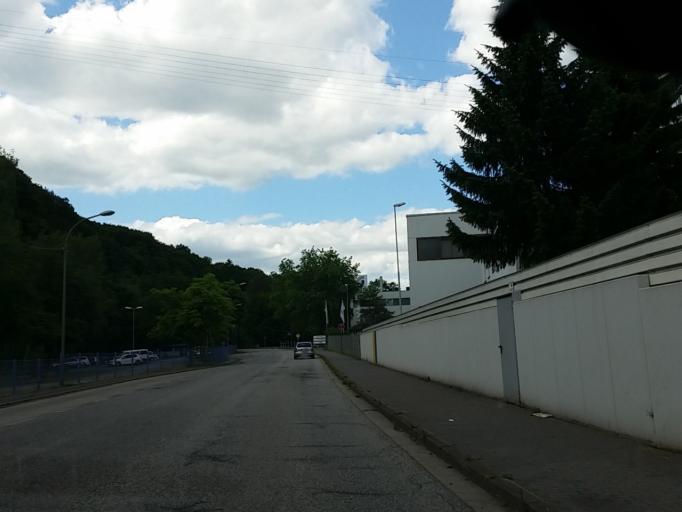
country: DE
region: Saarland
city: Wadern
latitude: 49.4978
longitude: 6.8672
